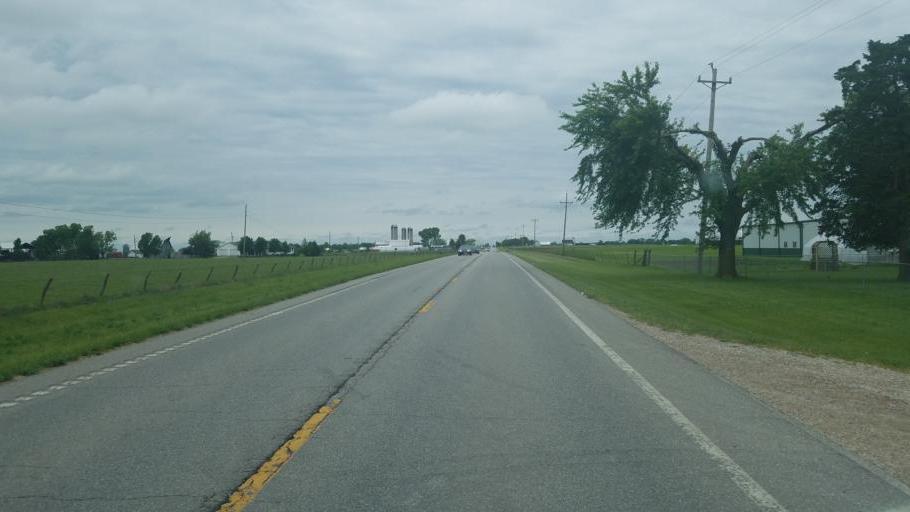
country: US
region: Missouri
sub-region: Morgan County
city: Versailles
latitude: 38.4748
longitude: -92.8087
